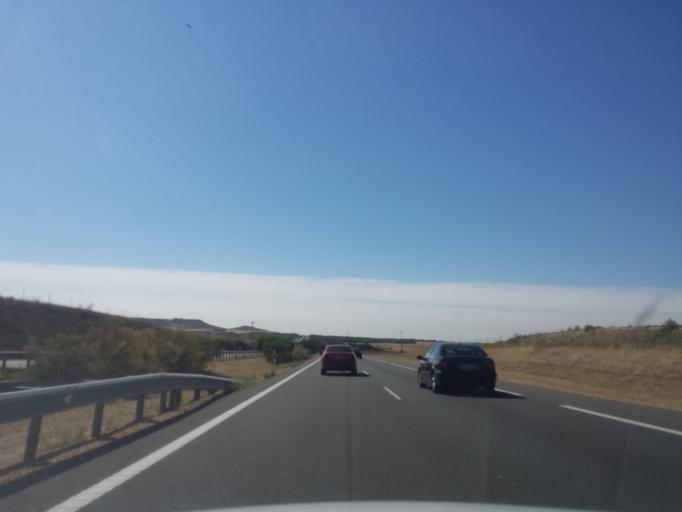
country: ES
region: Castille and Leon
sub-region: Provincia de Valladolid
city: Bercero
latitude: 41.5662
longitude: -5.0892
